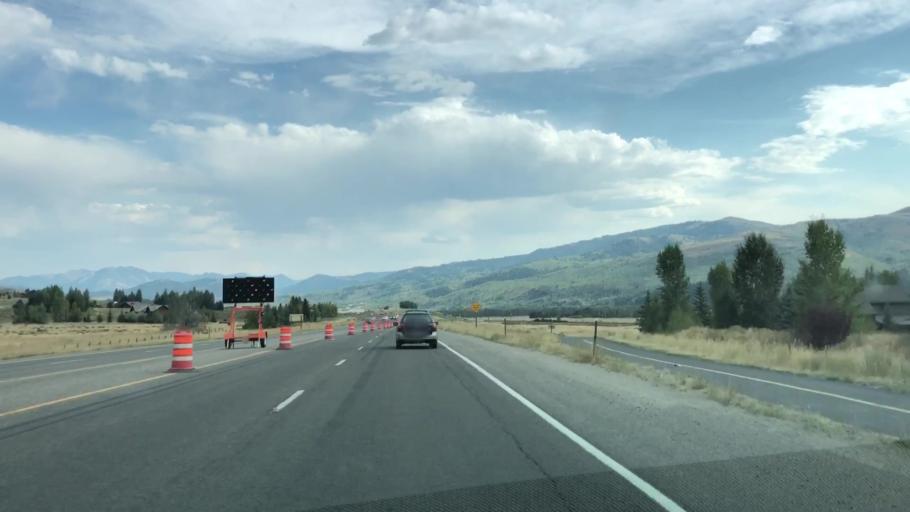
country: US
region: Wyoming
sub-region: Teton County
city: South Park
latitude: 43.4178
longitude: -110.7746
